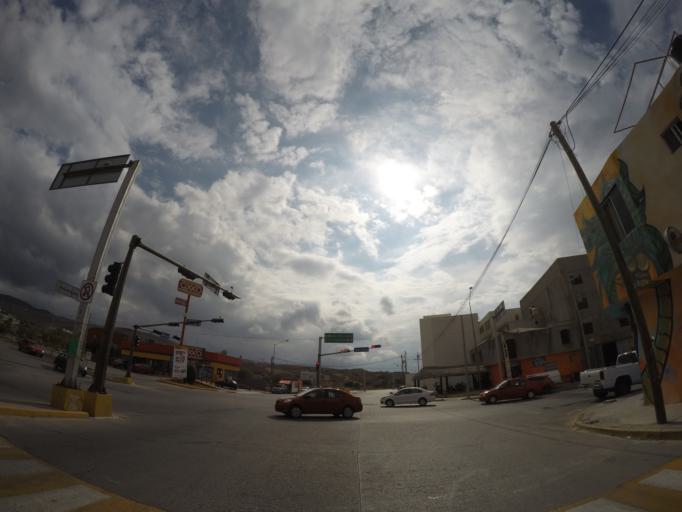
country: MX
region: San Luis Potosi
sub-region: San Luis Potosi
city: San Luis Potosi
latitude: 22.1238
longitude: -100.9858
